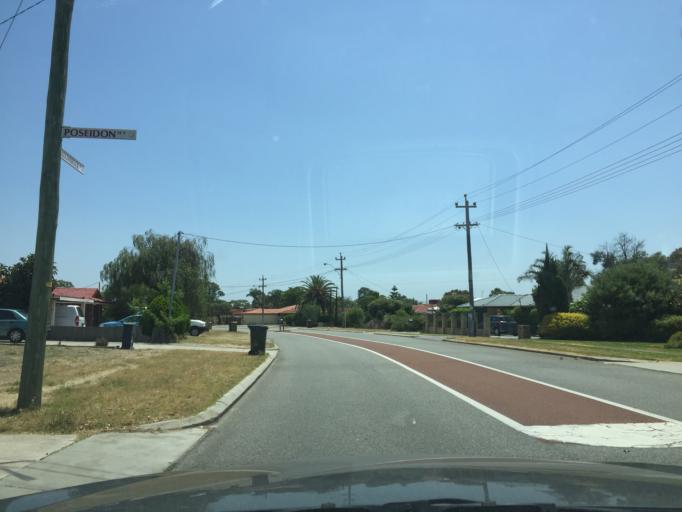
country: AU
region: Western Australia
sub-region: Canning
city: Ferndale
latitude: -32.0414
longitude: 115.9134
